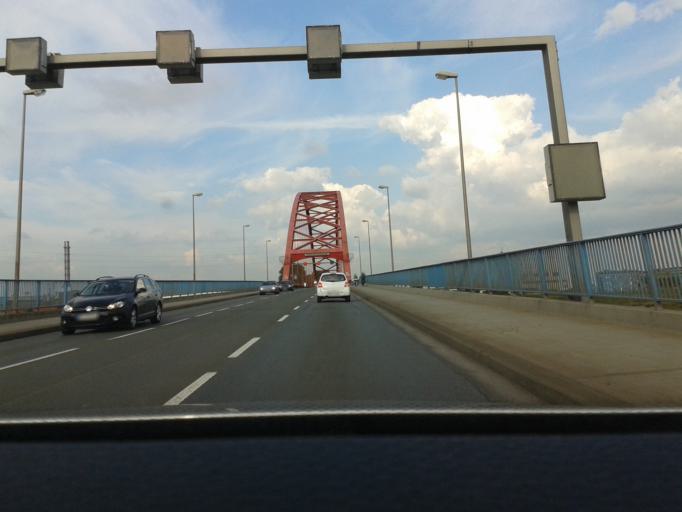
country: DE
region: North Rhine-Westphalia
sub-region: Regierungsbezirk Dusseldorf
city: Hochfeld
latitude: 51.4139
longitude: 6.7358
